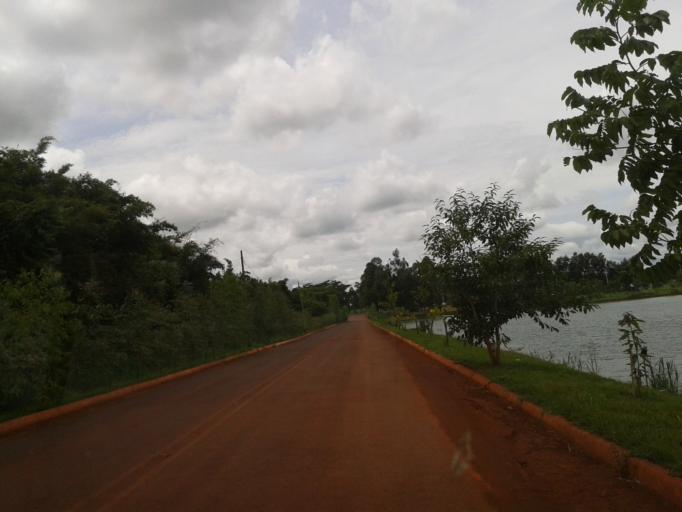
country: BR
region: Minas Gerais
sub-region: Centralina
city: Centralina
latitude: -18.5921
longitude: -49.2135
